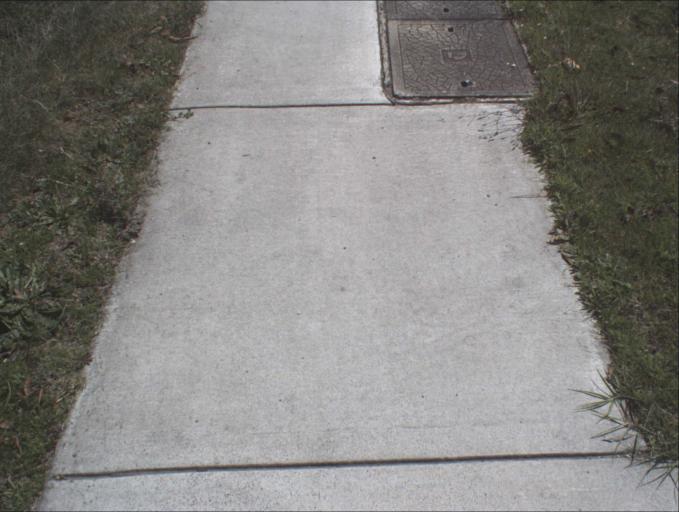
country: AU
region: Queensland
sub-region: Logan
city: Beenleigh
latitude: -27.7053
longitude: 153.1818
